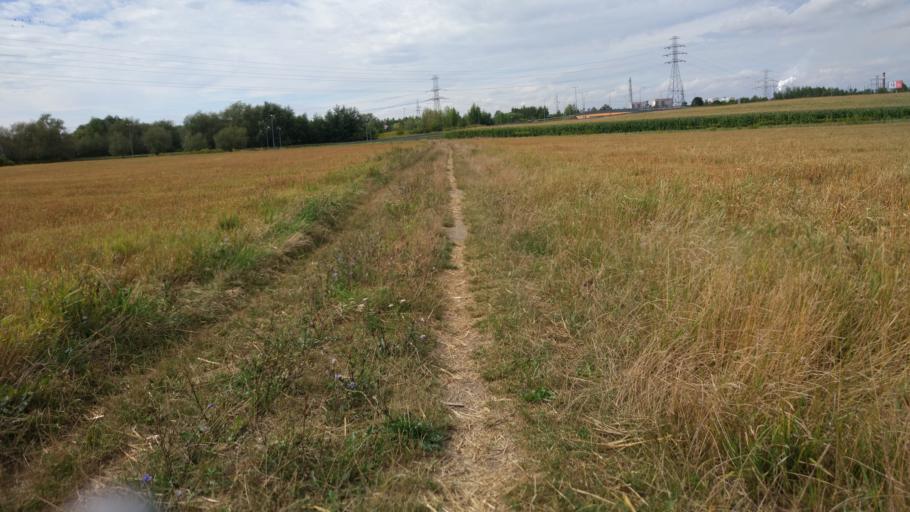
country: PL
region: Masovian Voivodeship
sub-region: Plock
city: Plock
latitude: 52.5295
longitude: 19.7418
